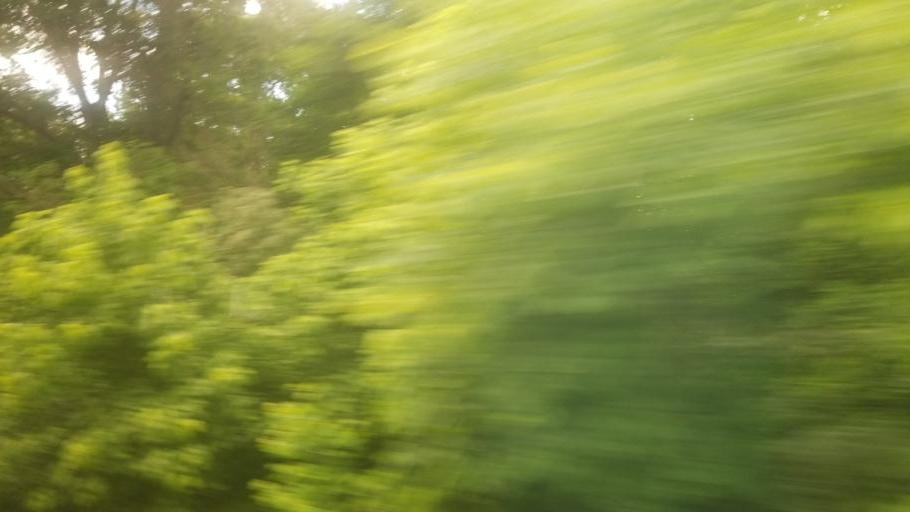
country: US
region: Maryland
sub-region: Frederick County
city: Brunswick
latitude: 39.3058
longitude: -77.6024
